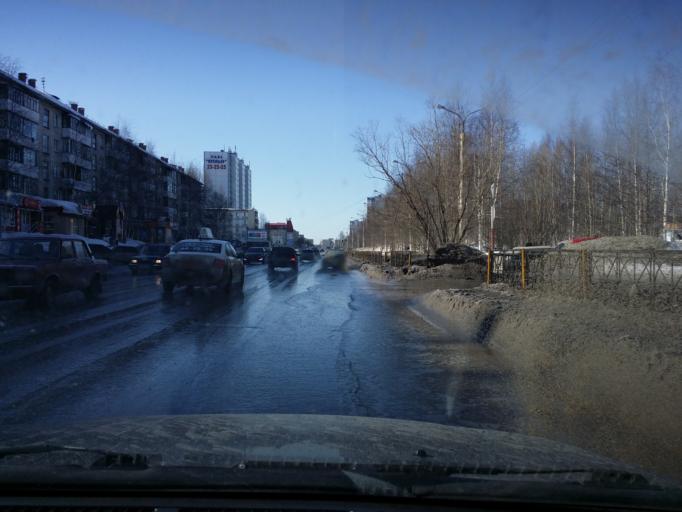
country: RU
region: Khanty-Mansiyskiy Avtonomnyy Okrug
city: Nizhnevartovsk
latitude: 60.9406
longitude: 76.5885
